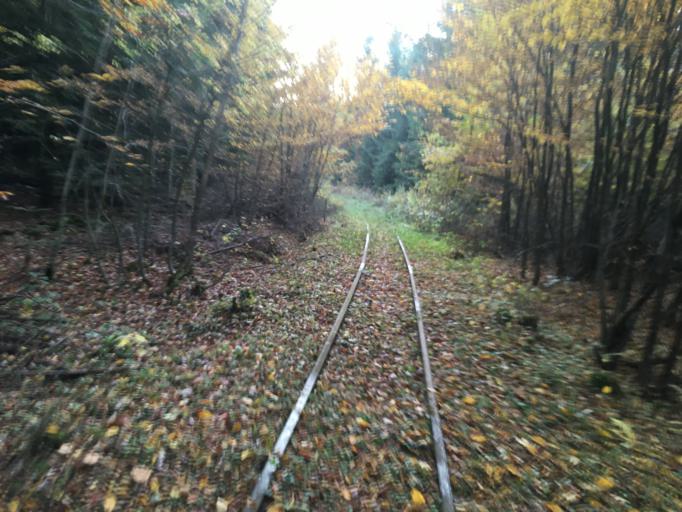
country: PL
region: Swietokrzyskie
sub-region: Powiat starachowicki
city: Brody
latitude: 51.0754
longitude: 21.1517
